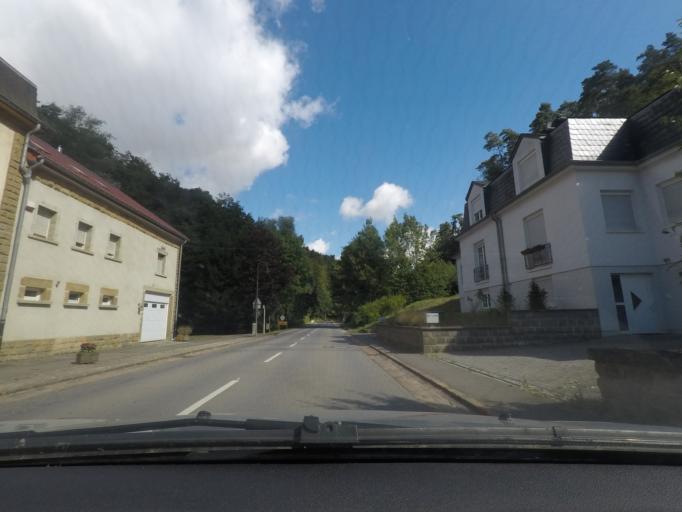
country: LU
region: Luxembourg
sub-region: Canton de Mersch
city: Heffingen
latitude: 49.7452
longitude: 6.2656
